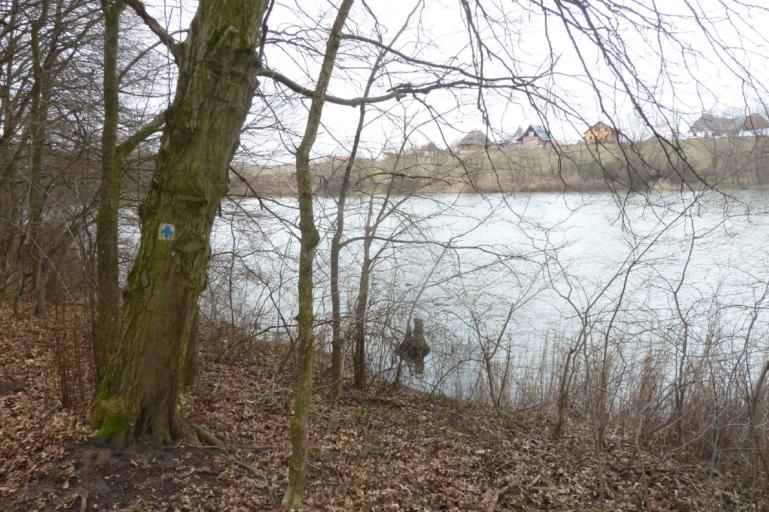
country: HU
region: Pest
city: Vacszentlaszlo
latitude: 47.6032
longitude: 19.5264
